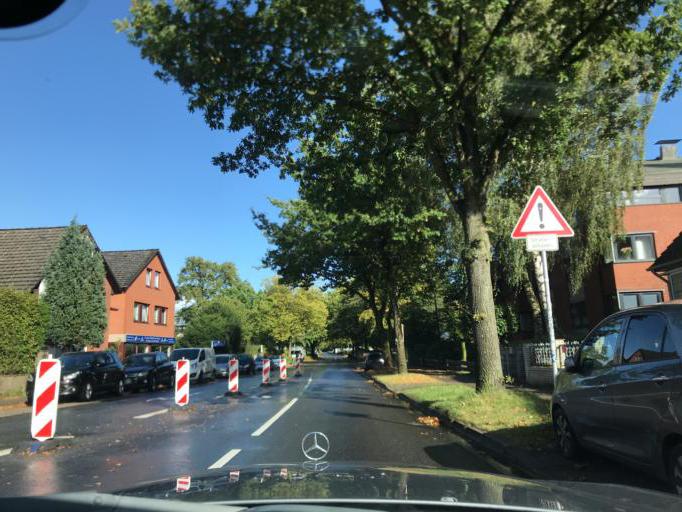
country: DE
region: Hamburg
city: Farmsen-Berne
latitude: 53.6202
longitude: 10.1497
